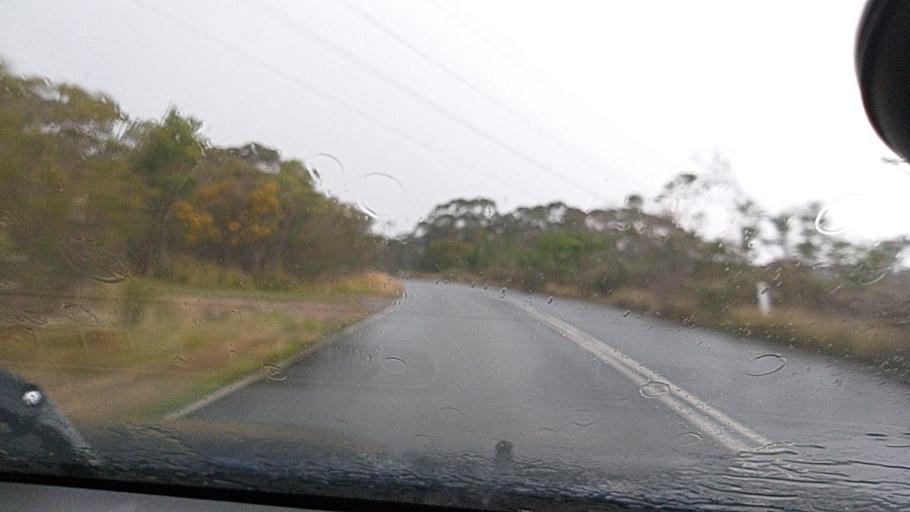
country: AU
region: New South Wales
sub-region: Wollongong
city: Mount Keira
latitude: -34.3915
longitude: 150.8410
